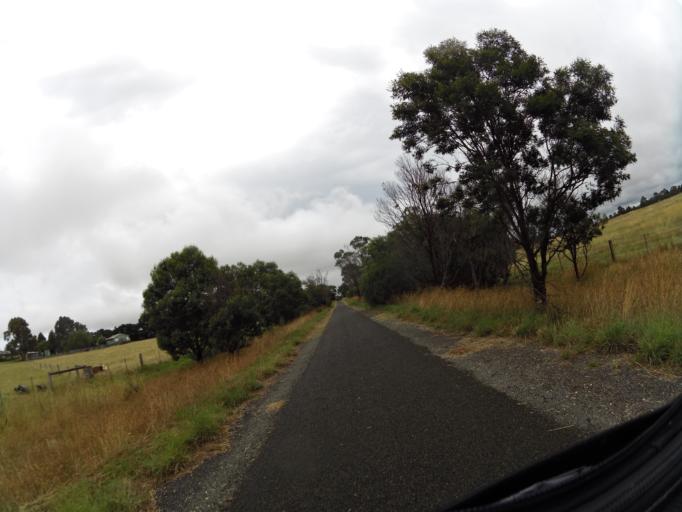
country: AU
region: Victoria
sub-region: East Gippsland
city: Bairnsdale
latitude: -37.8235
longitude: 147.7062
